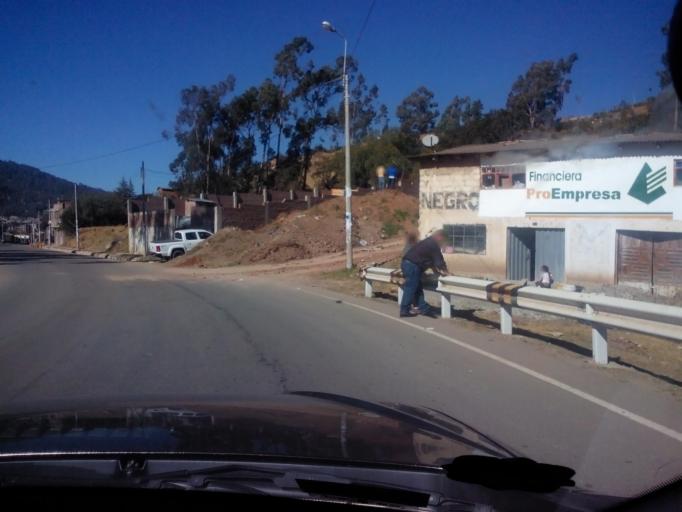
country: PE
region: Apurimac
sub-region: Provincia de Andahuaylas
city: Talavera
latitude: -13.6597
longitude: -73.4382
